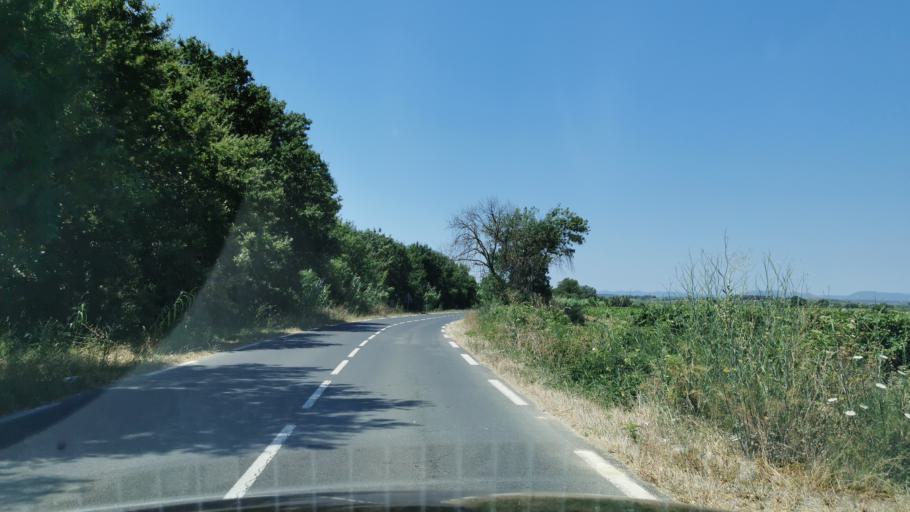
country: FR
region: Languedoc-Roussillon
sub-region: Departement de l'Herault
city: Maureilhan
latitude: 43.3643
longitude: 3.1202
